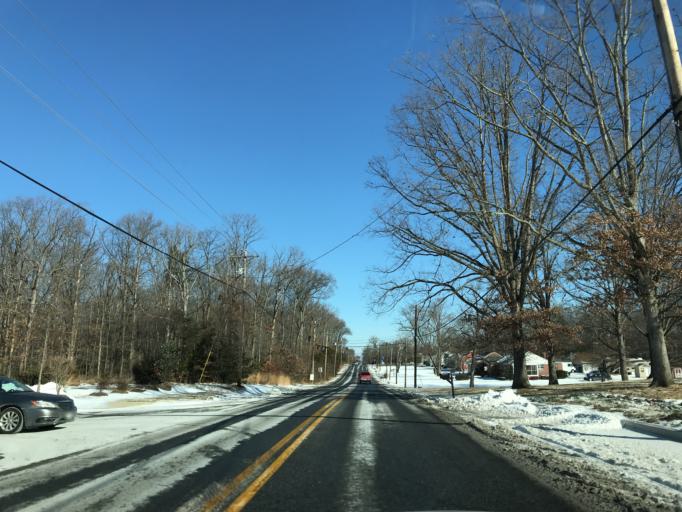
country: US
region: Maryland
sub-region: Charles County
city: Saint Charles
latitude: 38.6141
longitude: -76.9190
